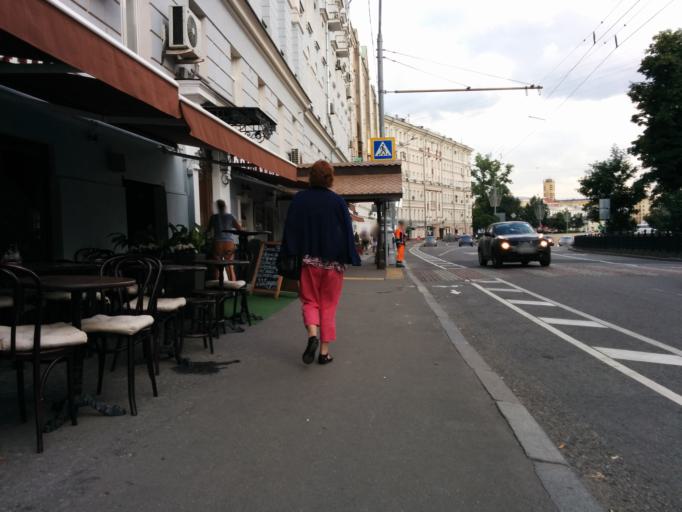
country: RU
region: Moscow
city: Moscow
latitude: 55.7554
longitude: 37.6002
